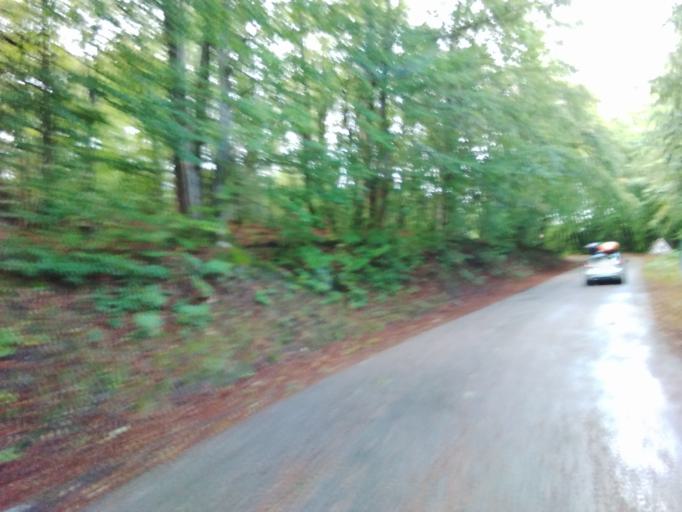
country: FR
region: Bourgogne
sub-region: Departement de la Nievre
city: Lormes
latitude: 47.2982
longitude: 3.8880
